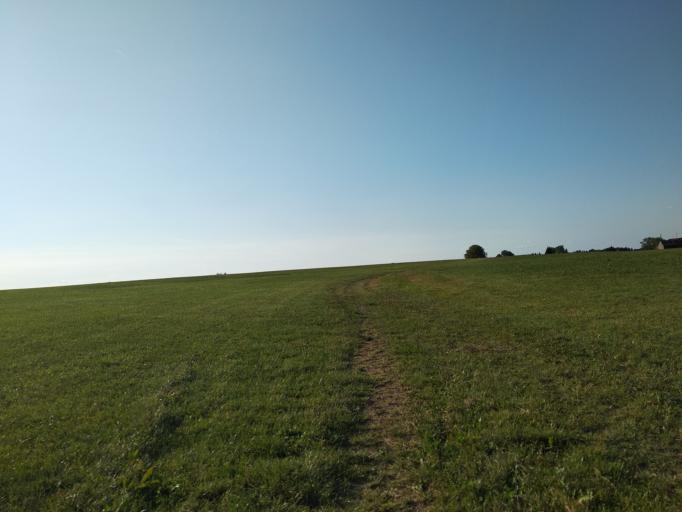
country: DE
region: Bavaria
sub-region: Swabia
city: Legau
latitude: 47.8593
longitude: 10.1188
